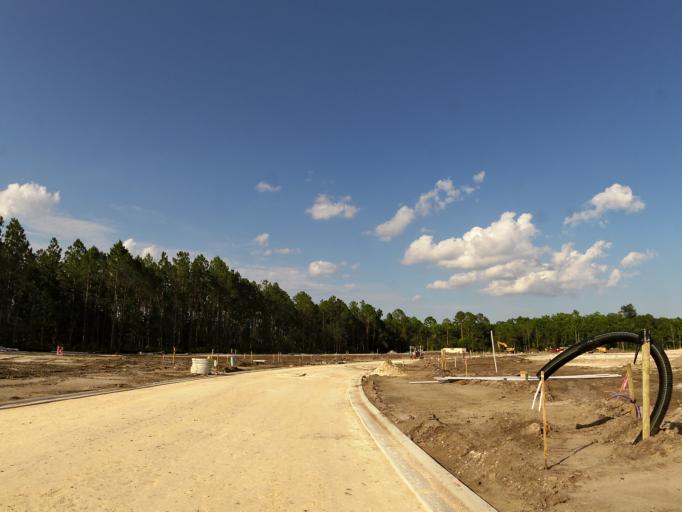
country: US
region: Florida
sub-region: Clay County
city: Green Cove Springs
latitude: 30.0342
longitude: -81.6314
